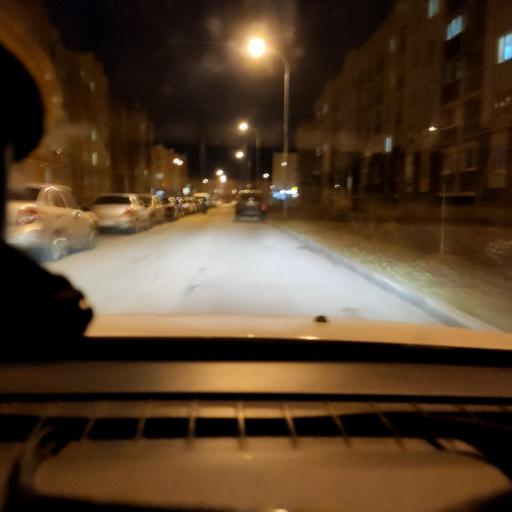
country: RU
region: Samara
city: Samara
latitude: 53.1183
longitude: 50.1569
